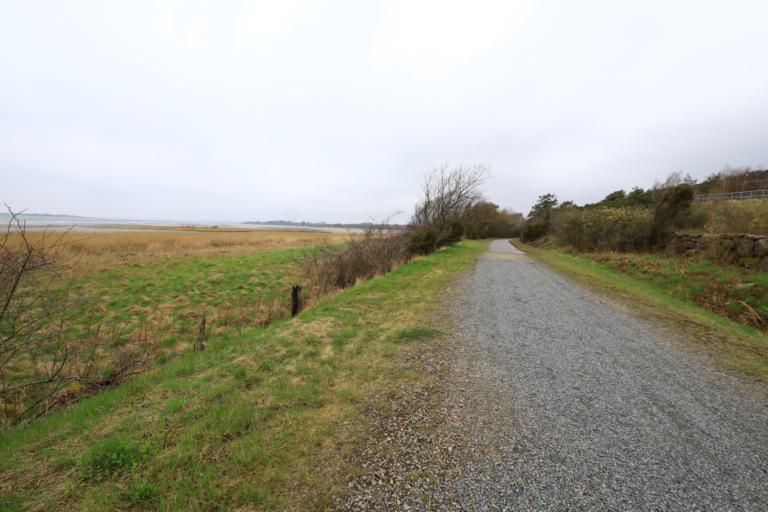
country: SE
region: Halland
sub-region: Kungsbacka Kommun
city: Frillesas
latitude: 57.3028
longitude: 12.1681
